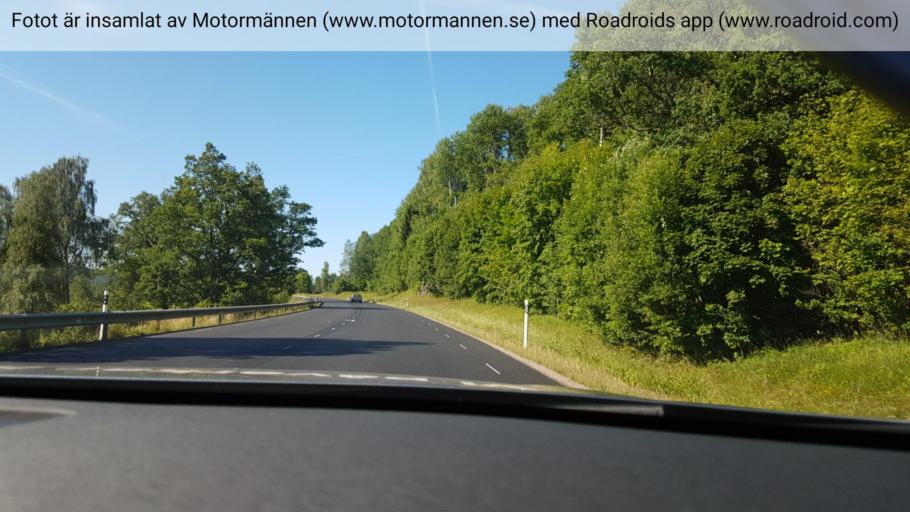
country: SE
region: Vaestra Goetaland
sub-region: Ulricehamns Kommun
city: Ulricehamn
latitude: 57.9112
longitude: 13.4784
